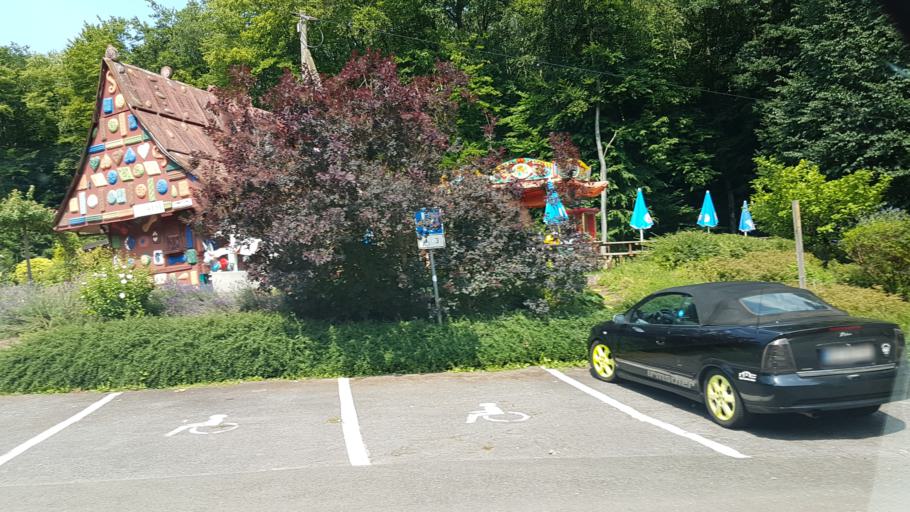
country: DE
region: Saarland
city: Neunkirchen
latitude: 49.3452
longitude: 7.2052
